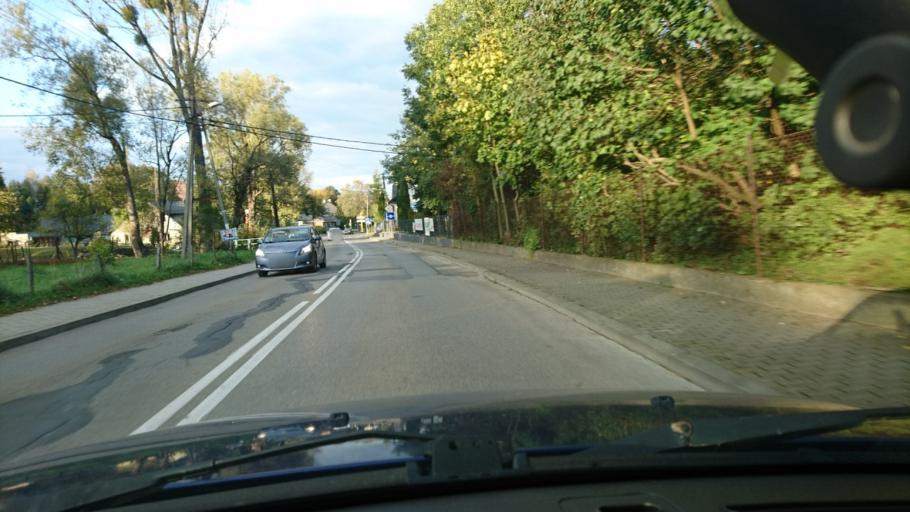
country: PL
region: Silesian Voivodeship
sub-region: Bielsko-Biala
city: Bielsko-Biala
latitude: 49.7968
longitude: 19.0151
